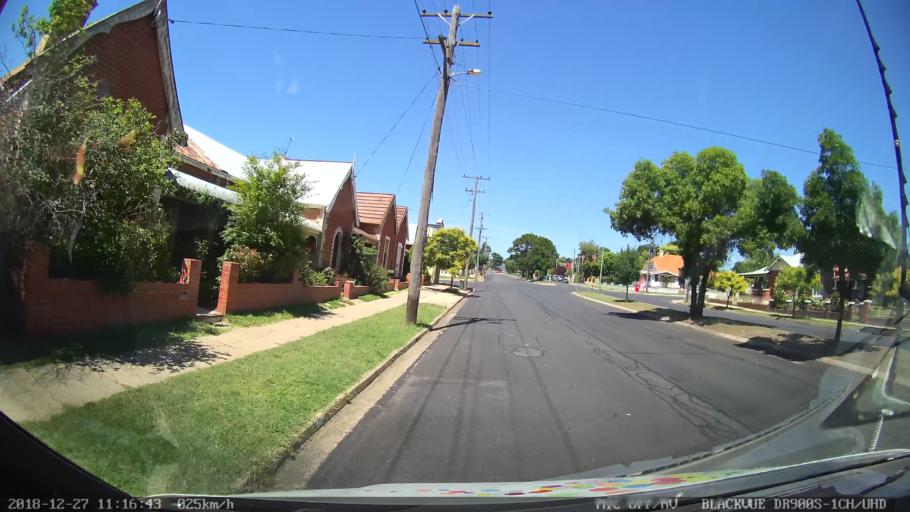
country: AU
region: New South Wales
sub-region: Bathurst Regional
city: Bathurst
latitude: -33.4226
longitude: 149.5740
